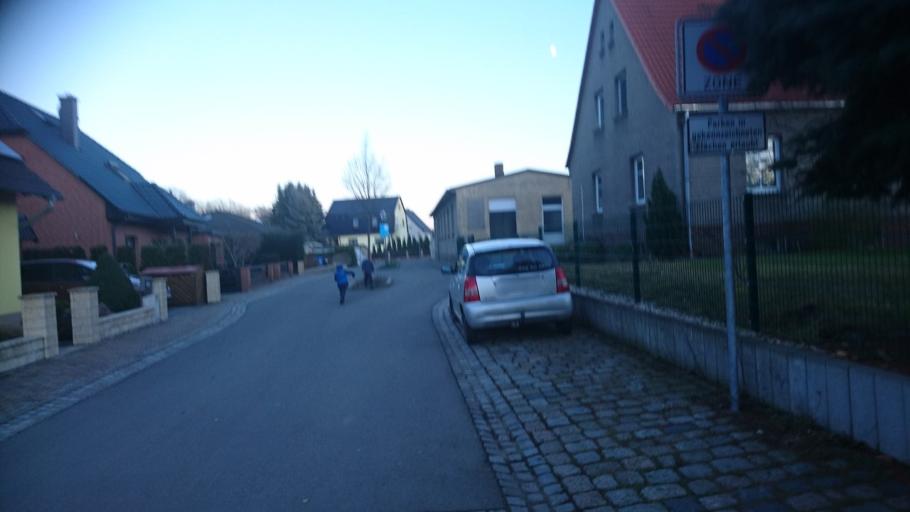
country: DE
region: Saxony
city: Bad Duben
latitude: 51.5925
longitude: 12.5868
